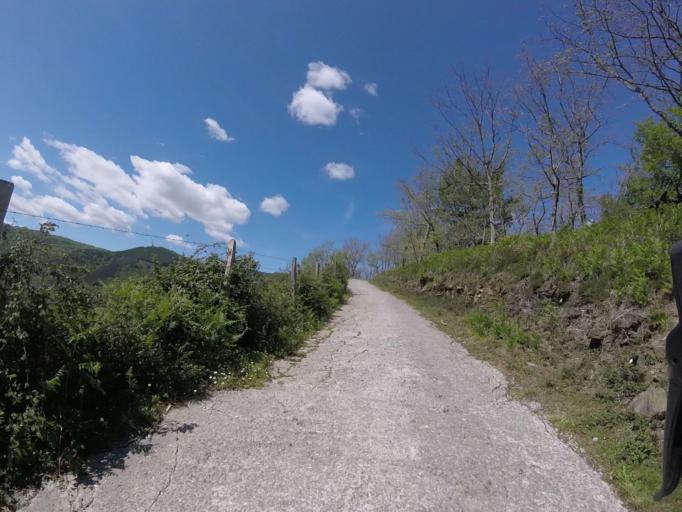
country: ES
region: Navarre
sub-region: Provincia de Navarra
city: Lesaka
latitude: 43.2430
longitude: -1.7415
